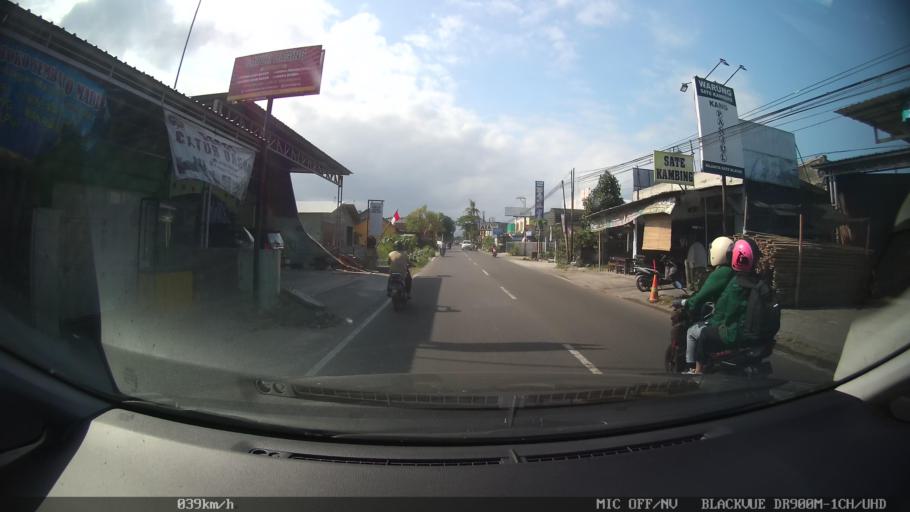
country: ID
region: Daerah Istimewa Yogyakarta
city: Sewon
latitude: -7.8588
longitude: 110.3896
